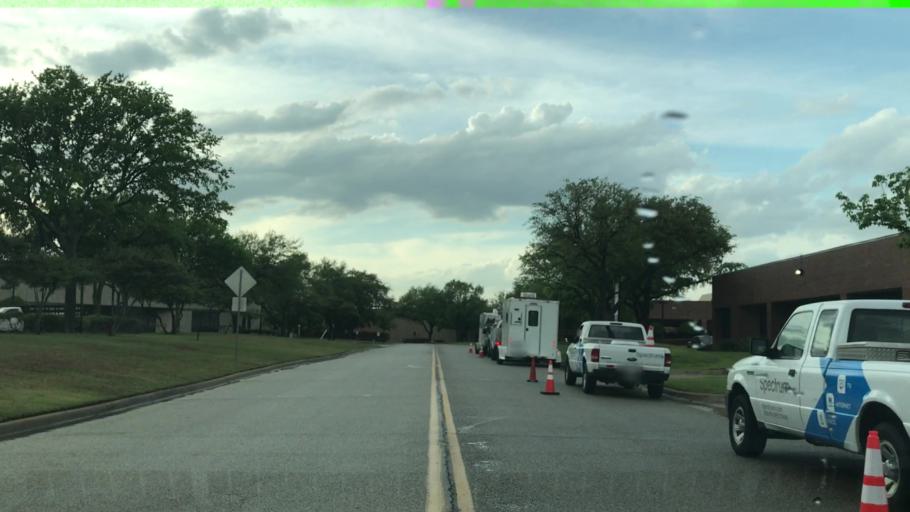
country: US
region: Texas
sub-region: Dallas County
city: Irving
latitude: 32.8729
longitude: -96.9833
